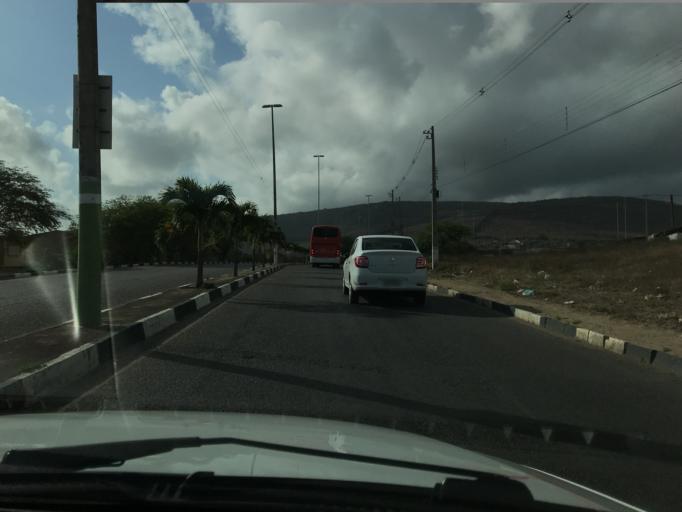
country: BR
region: Pernambuco
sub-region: Bezerros
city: Bezerros
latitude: -8.2358
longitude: -35.7427
